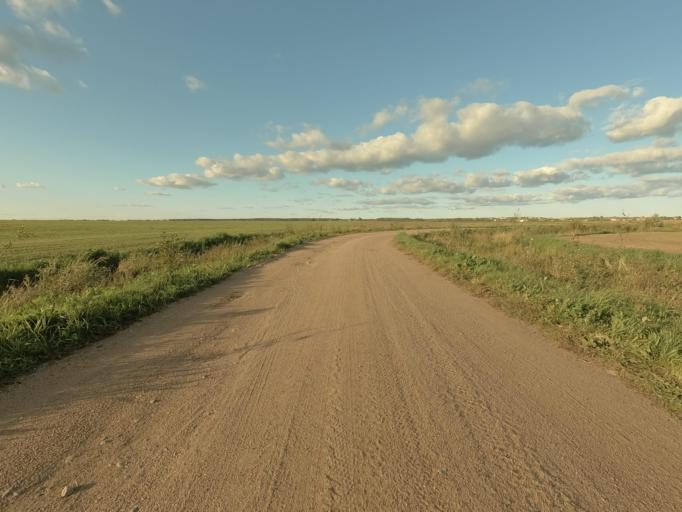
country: RU
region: Leningrad
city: Otradnoye
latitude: 59.8619
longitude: 30.7520
